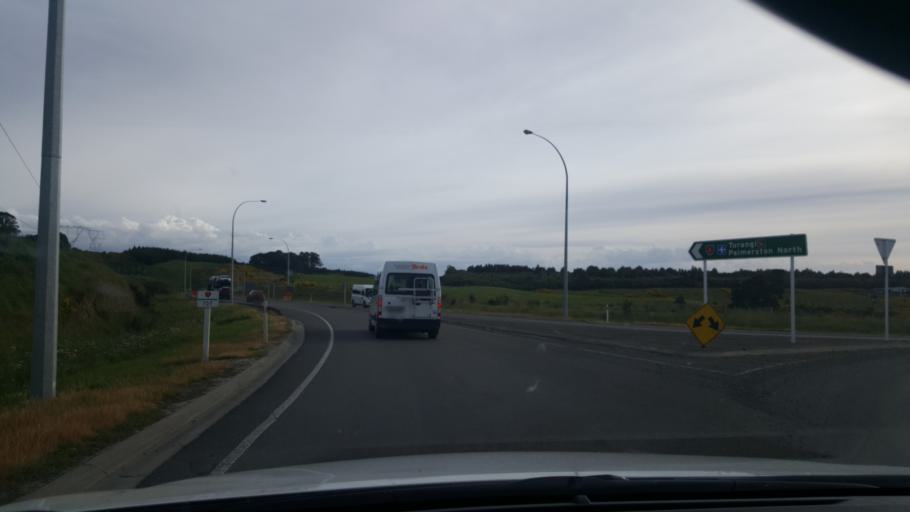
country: NZ
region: Waikato
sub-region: Taupo District
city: Taupo
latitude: -38.7045
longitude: 176.1123
